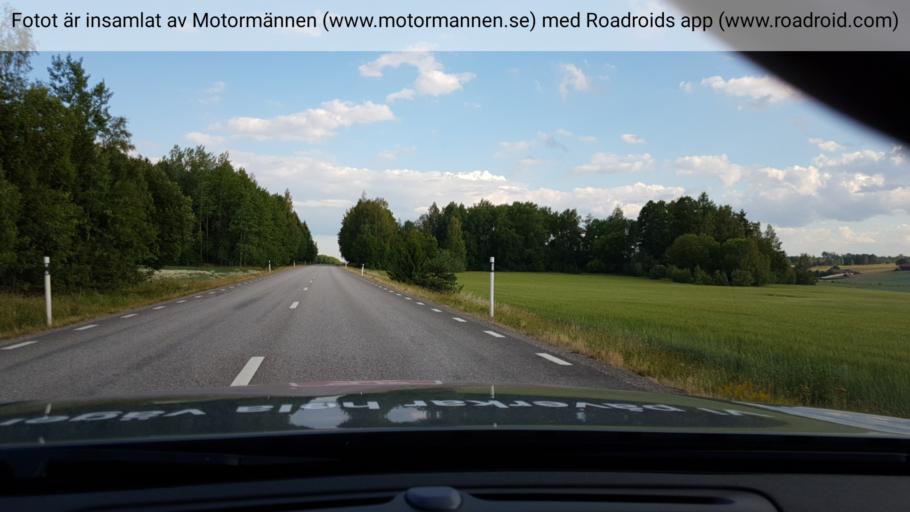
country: SE
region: Uppsala
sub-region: Heby Kommun
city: Heby
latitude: 59.9083
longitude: 16.8928
